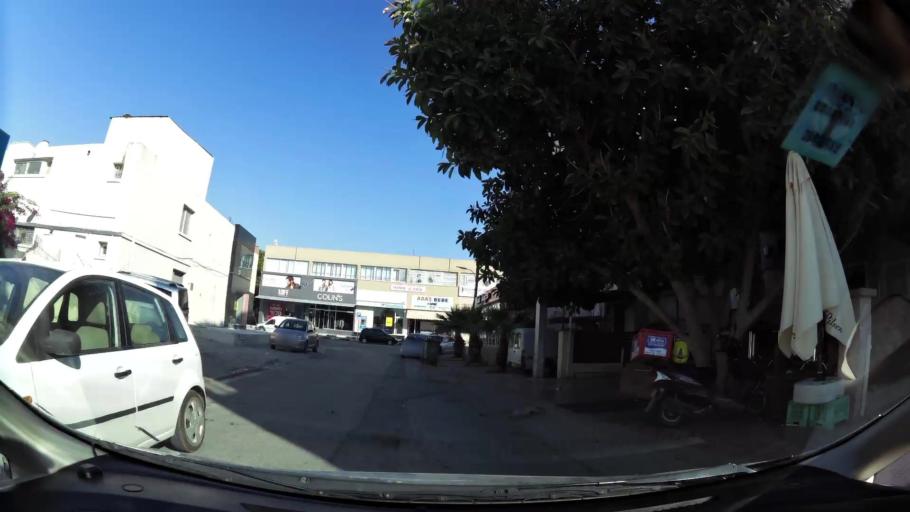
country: CY
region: Lefkosia
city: Nicosia
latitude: 35.2064
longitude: 33.3411
